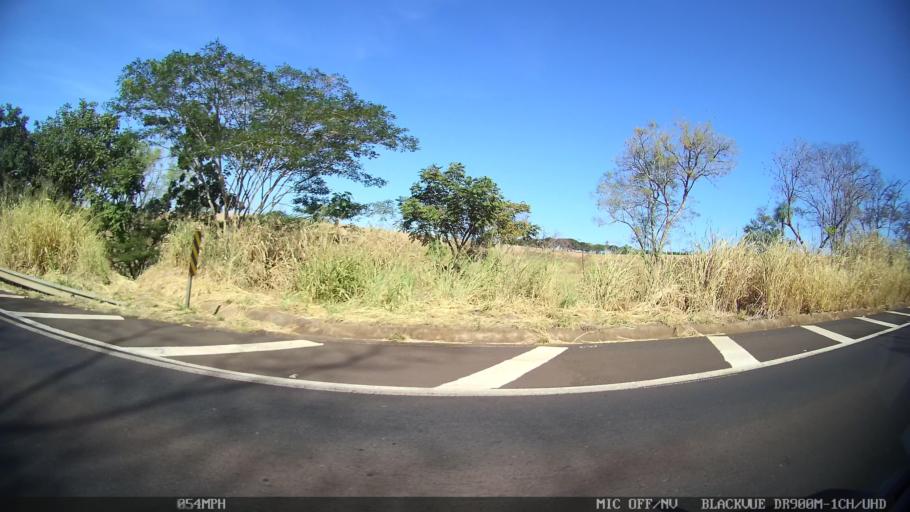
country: BR
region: Sao Paulo
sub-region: Barretos
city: Barretos
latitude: -20.6044
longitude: -48.7363
